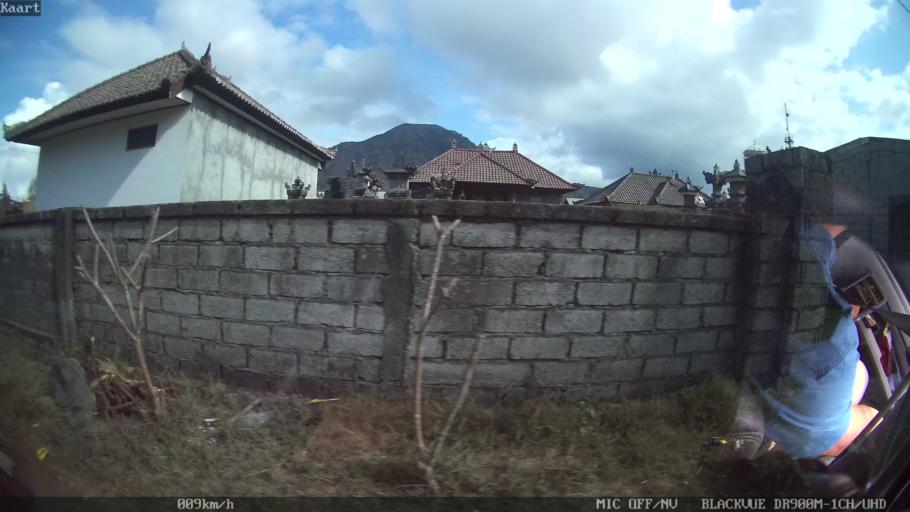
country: ID
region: Bali
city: Banjar Trunyan
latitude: -8.2156
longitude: 115.3772
